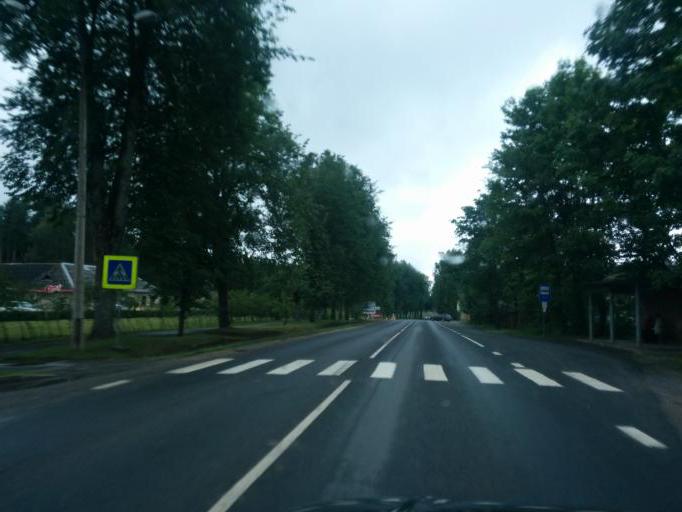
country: LV
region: Smiltene
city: Smiltene
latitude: 57.4089
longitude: 25.9414
